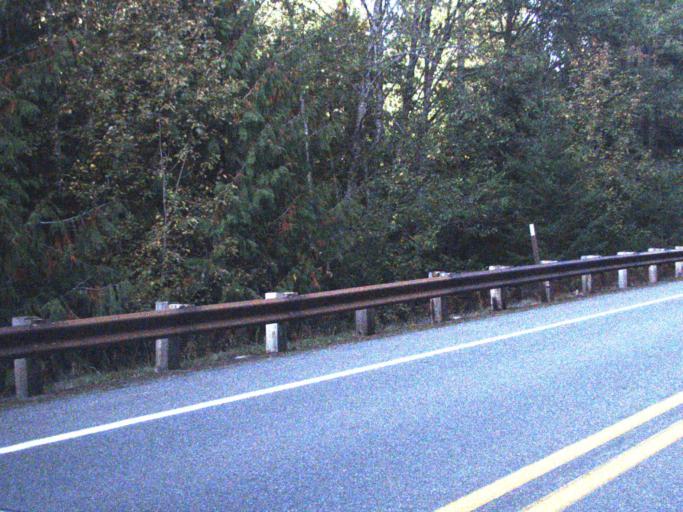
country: US
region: Washington
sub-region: Snohomish County
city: Darrington
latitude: 48.7054
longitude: -120.9358
